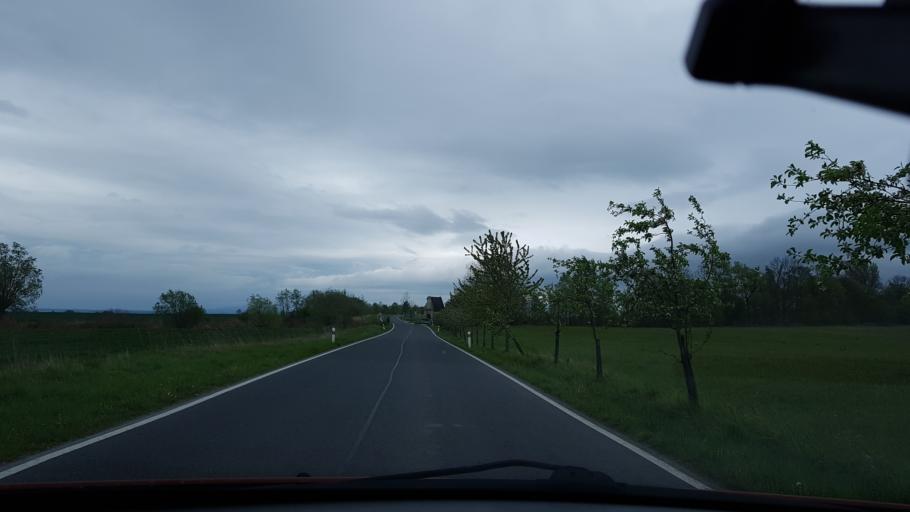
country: PL
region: Opole Voivodeship
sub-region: Powiat nyski
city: Kamienica
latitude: 50.4236
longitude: 16.9674
